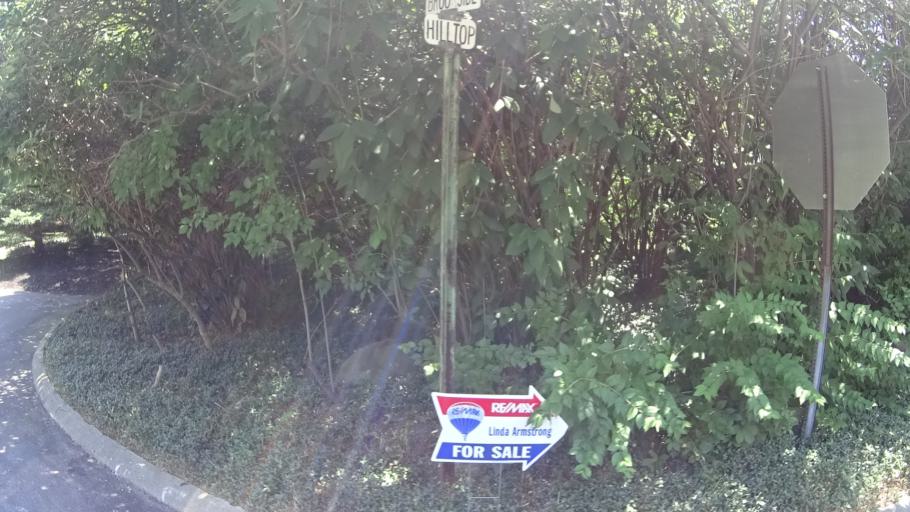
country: US
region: Ohio
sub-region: Erie County
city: Sandusky
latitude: 41.4087
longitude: -82.6410
